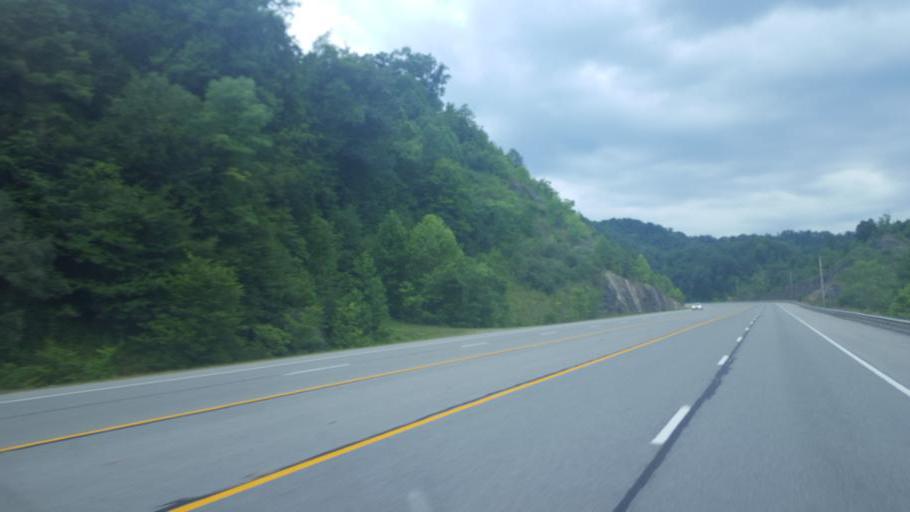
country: US
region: Kentucky
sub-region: Letcher County
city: Jenkins
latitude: 37.2779
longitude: -82.5848
